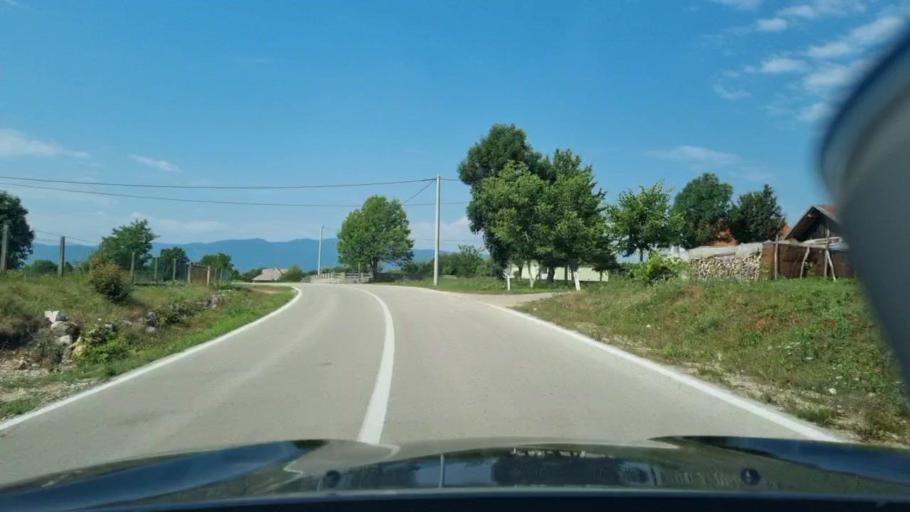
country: BA
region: Federation of Bosnia and Herzegovina
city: Ostrozac
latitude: 44.8806
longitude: 15.9069
